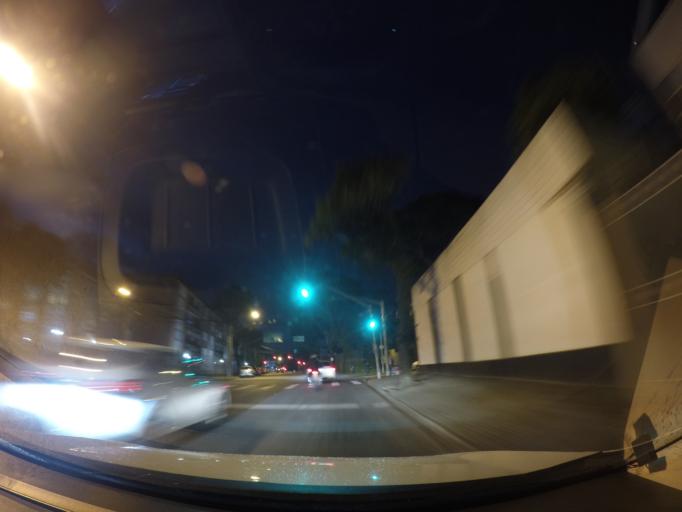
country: BR
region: Parana
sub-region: Curitiba
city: Curitiba
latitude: -25.4581
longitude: -49.2685
